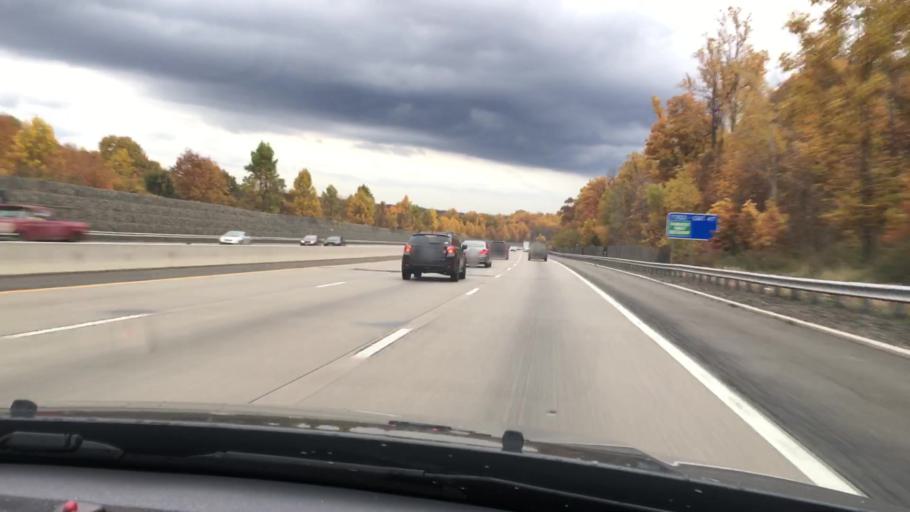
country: US
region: New Jersey
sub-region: Morris County
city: Lincoln Park
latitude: 40.9455
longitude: -74.3460
